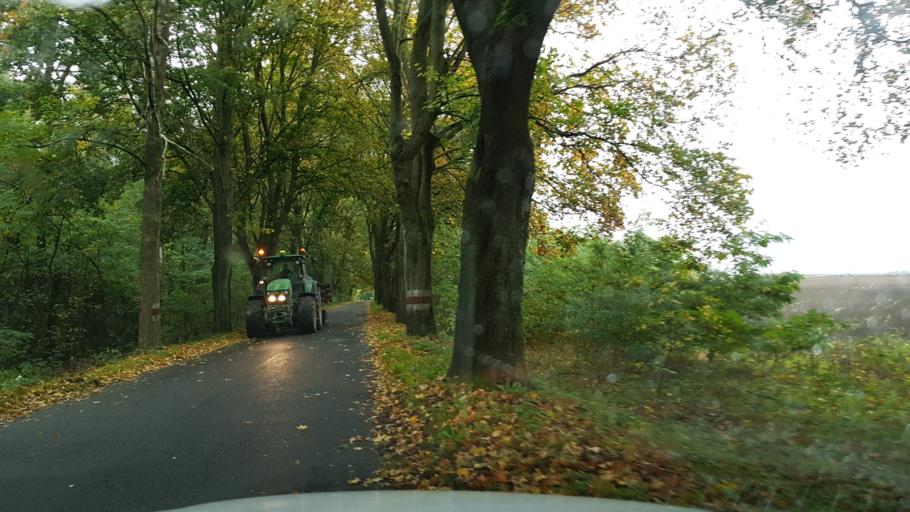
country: PL
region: West Pomeranian Voivodeship
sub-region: Powiat mysliborski
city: Mysliborz
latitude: 52.9909
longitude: 14.8618
